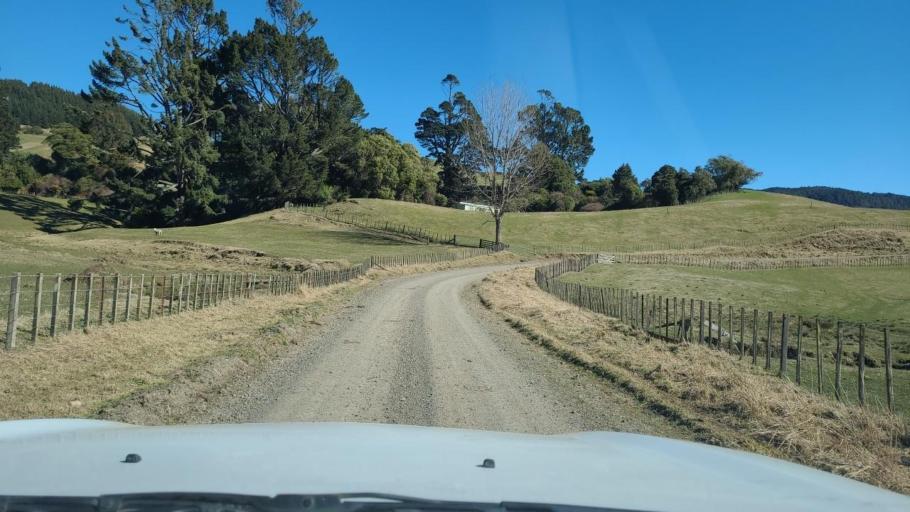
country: NZ
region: Hawke's Bay
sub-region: Napier City
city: Taradale
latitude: -39.2830
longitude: 176.4838
